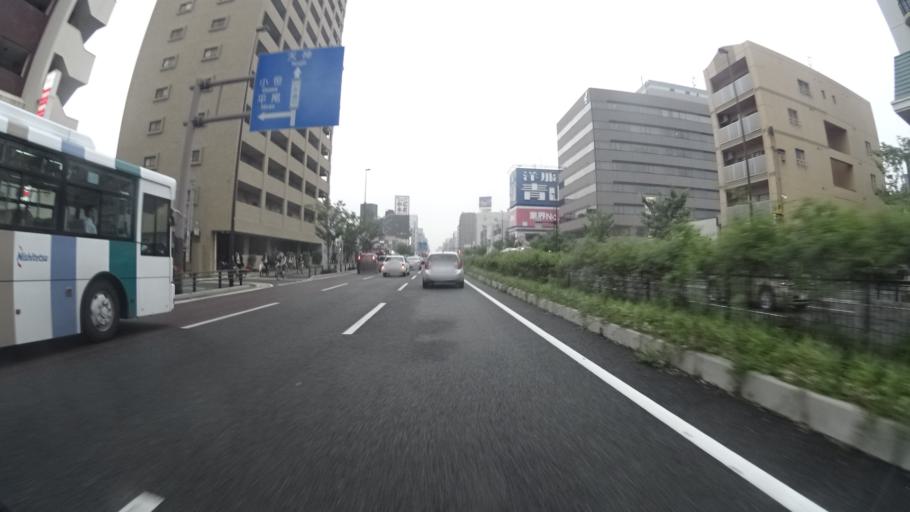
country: JP
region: Fukuoka
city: Fukuoka-shi
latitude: 33.5741
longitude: 130.4135
